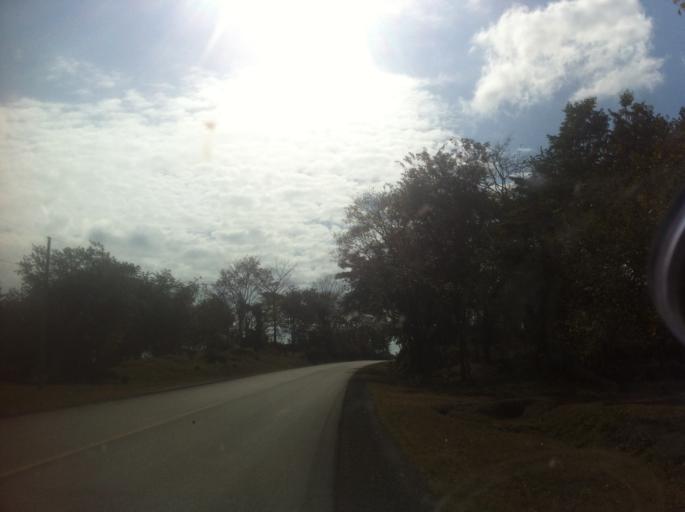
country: NI
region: Rio San Juan
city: San Miguelito
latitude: 11.3940
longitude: -84.8029
